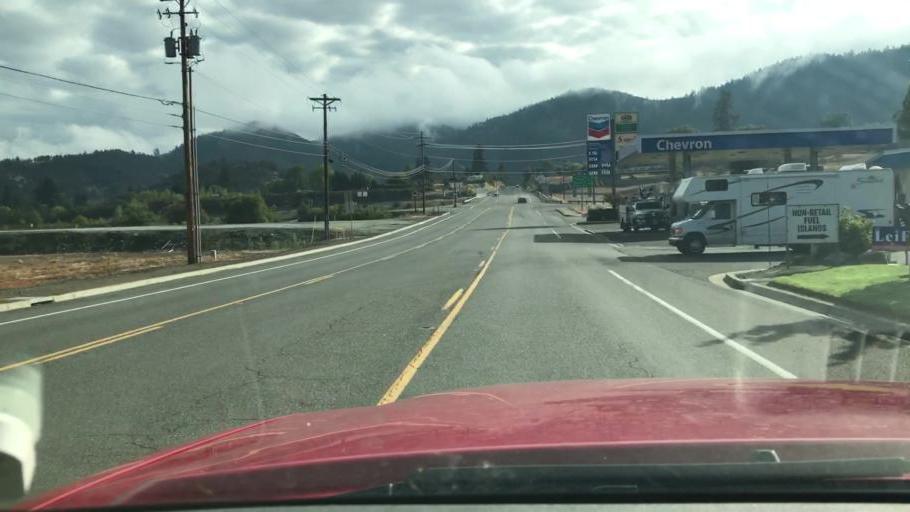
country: US
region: Oregon
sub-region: Douglas County
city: Tri-City
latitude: 42.9733
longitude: -123.3395
